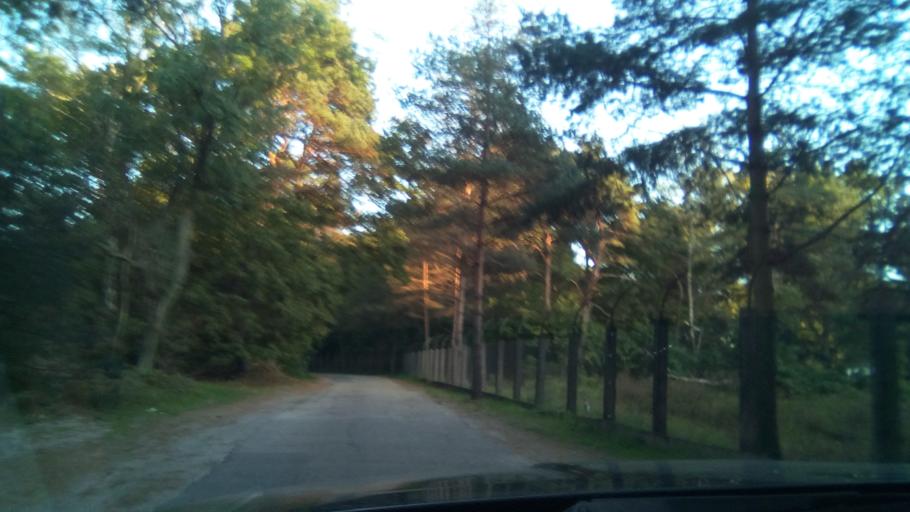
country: PL
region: West Pomeranian Voivodeship
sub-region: Swinoujscie
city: Swinoujscie
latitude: 53.9183
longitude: 14.2886
